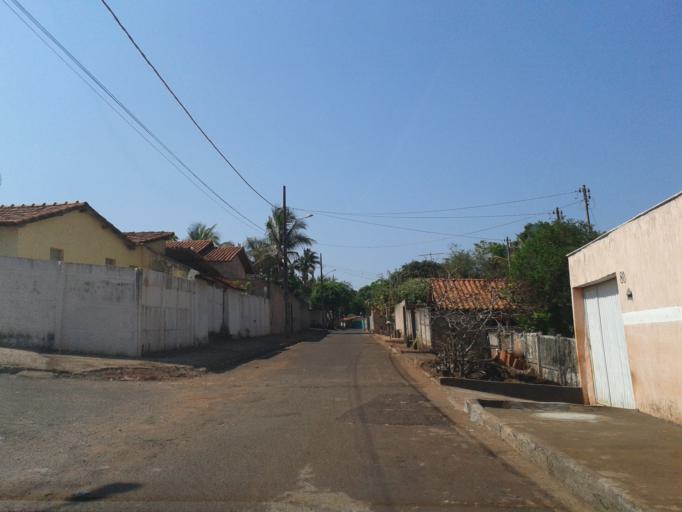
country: BR
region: Minas Gerais
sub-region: Ituiutaba
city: Ituiutaba
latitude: -18.9562
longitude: -49.4538
